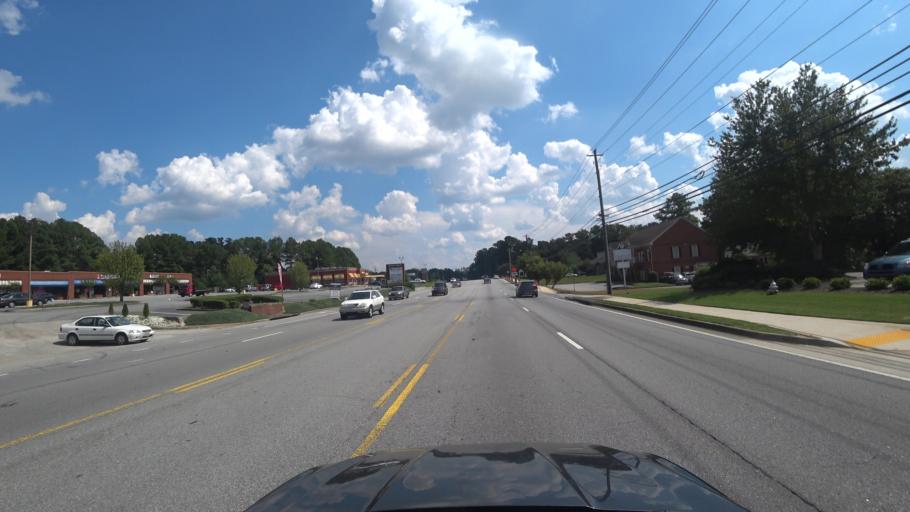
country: US
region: Georgia
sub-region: Gwinnett County
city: Norcross
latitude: 33.9544
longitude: -84.2440
